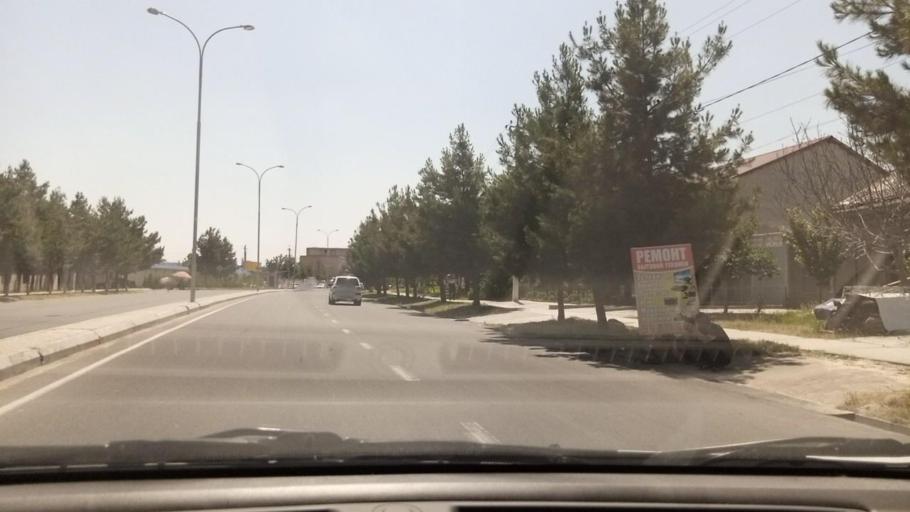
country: UZ
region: Toshkent Shahri
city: Tashkent
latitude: 41.2296
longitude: 69.1835
